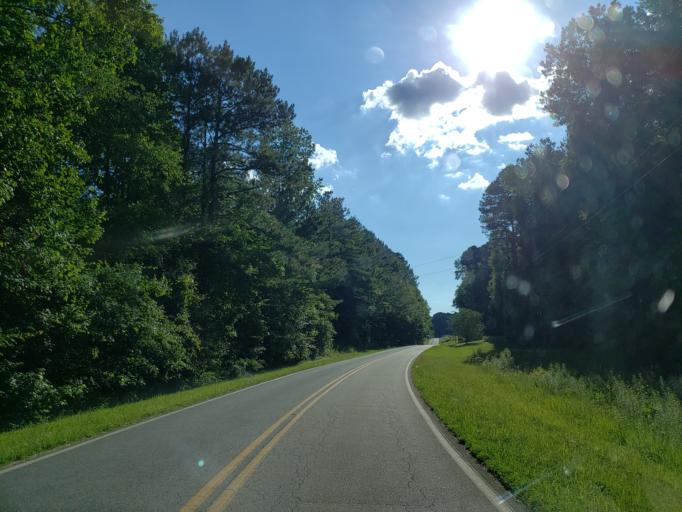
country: US
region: Georgia
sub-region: Carroll County
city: Carrollton
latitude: 33.6500
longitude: -85.1040
